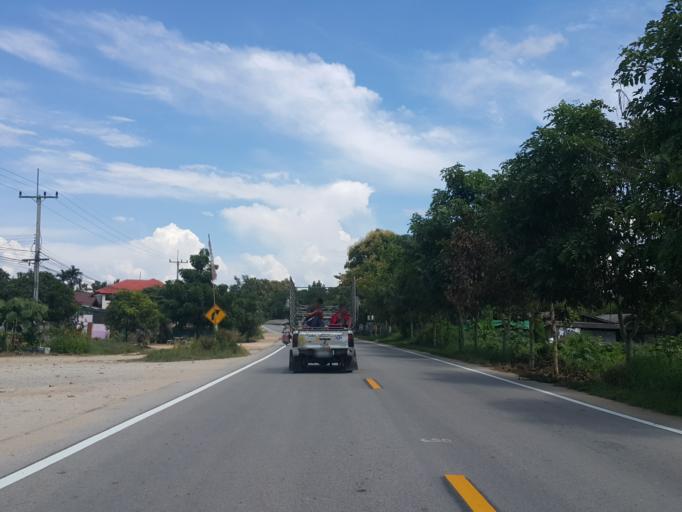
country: TH
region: Chiang Mai
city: Phrao
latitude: 19.2521
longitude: 99.1846
